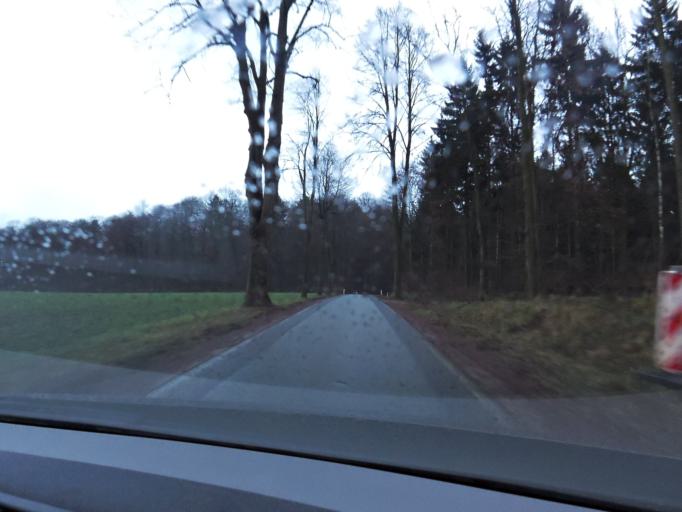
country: DE
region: Schleswig-Holstein
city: Salem
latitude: 53.6624
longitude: 10.8586
